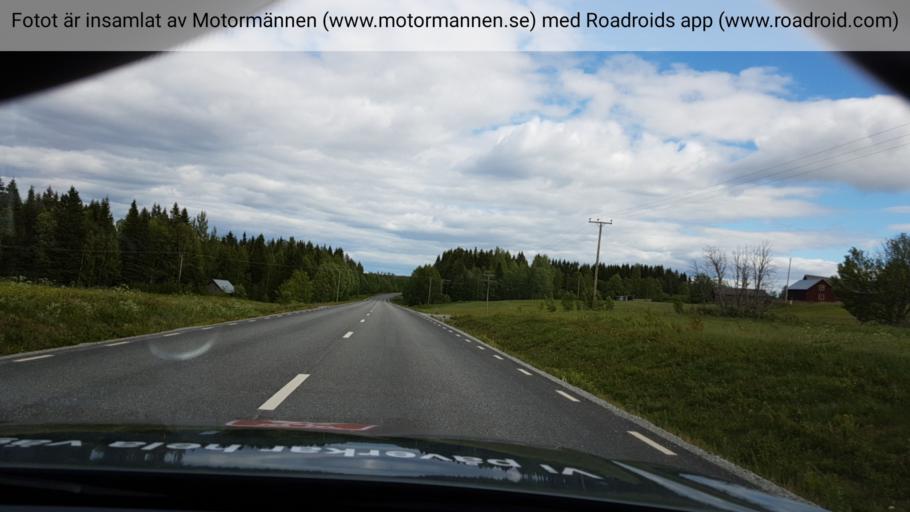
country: SE
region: Jaemtland
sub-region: Stroemsunds Kommun
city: Stroemsund
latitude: 64.2146
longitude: 15.5647
